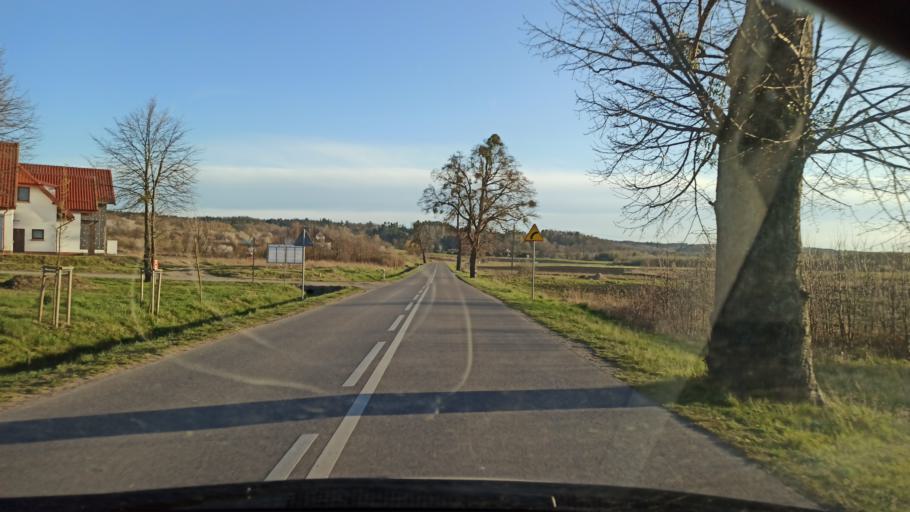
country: PL
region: Warmian-Masurian Voivodeship
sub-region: Powiat elblaski
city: Tolkmicko
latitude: 54.3135
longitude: 19.5206
